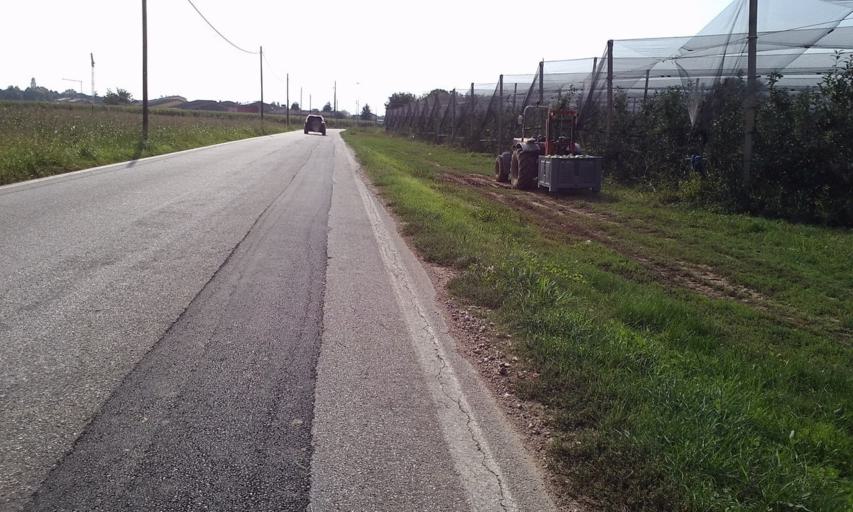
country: IT
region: Veneto
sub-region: Provincia di Verona
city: Povegliano Veronese
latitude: 45.3572
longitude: 10.8867
